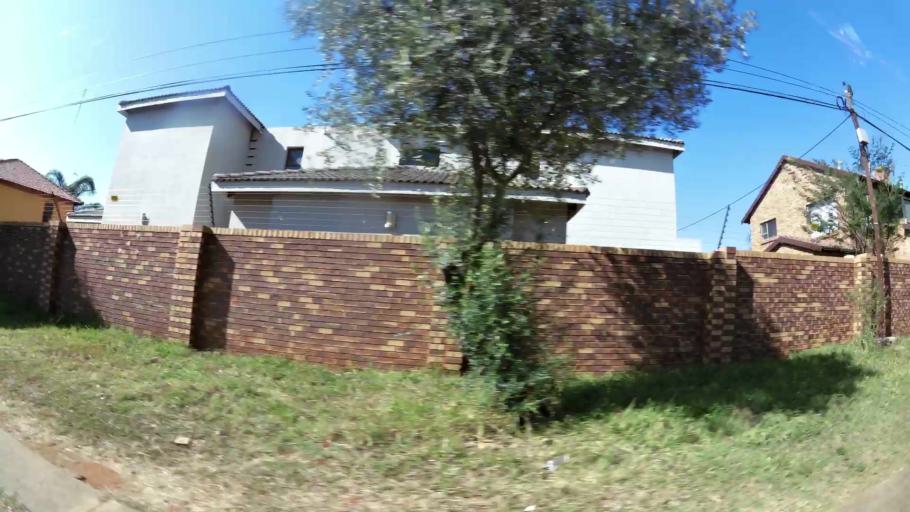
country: ZA
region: Gauteng
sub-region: City of Tshwane Metropolitan Municipality
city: Pretoria
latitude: -25.6592
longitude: 28.2504
